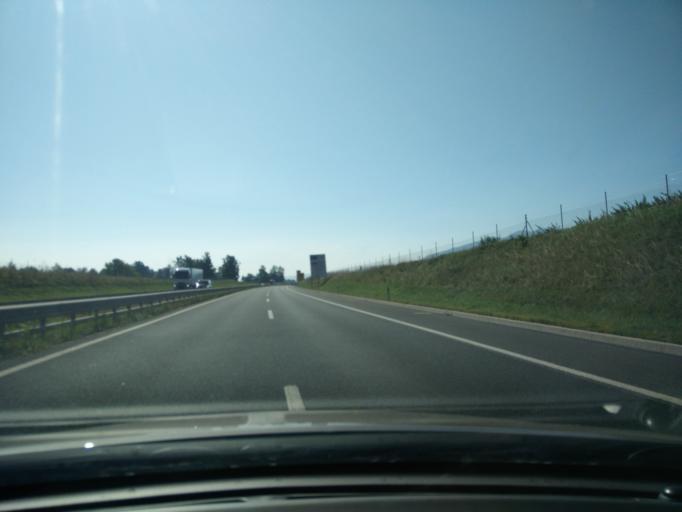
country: SI
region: Radovljica
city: Lesce
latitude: 46.3782
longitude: 14.1520
